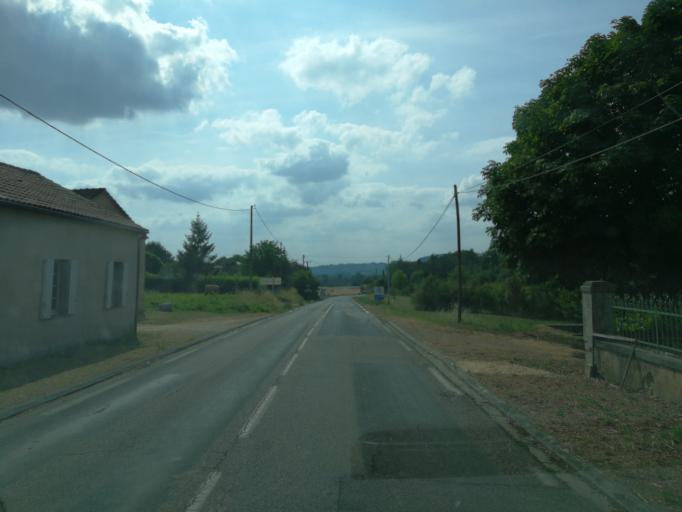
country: FR
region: Aquitaine
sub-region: Departement du Lot-et-Garonne
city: Montayral
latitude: 44.4896
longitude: 1.0129
